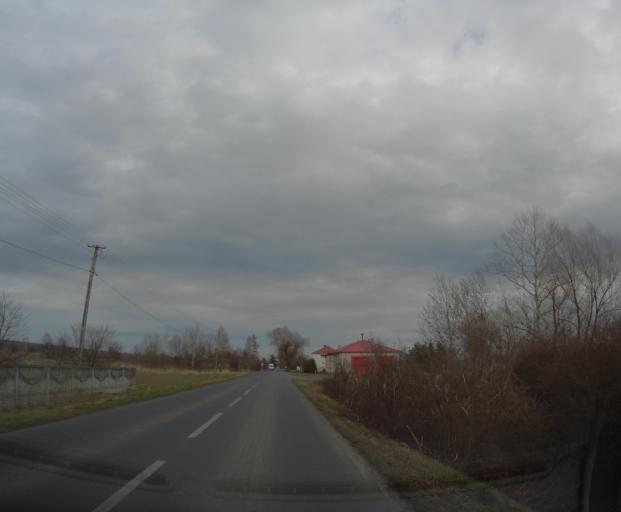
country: PL
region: Subcarpathian Voivodeship
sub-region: Powiat nizanski
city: Ulanow
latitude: 50.4752
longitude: 22.2507
